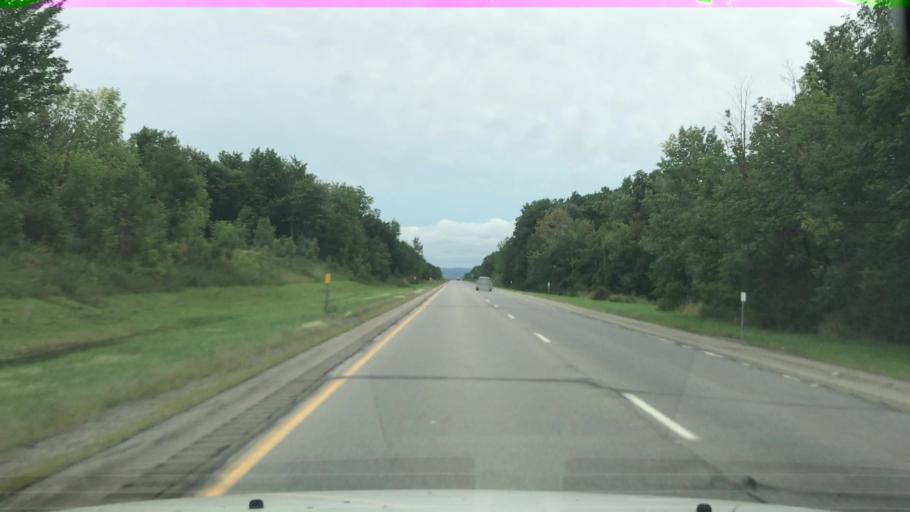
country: US
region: New York
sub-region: Erie County
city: Springville
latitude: 42.5349
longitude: -78.7062
